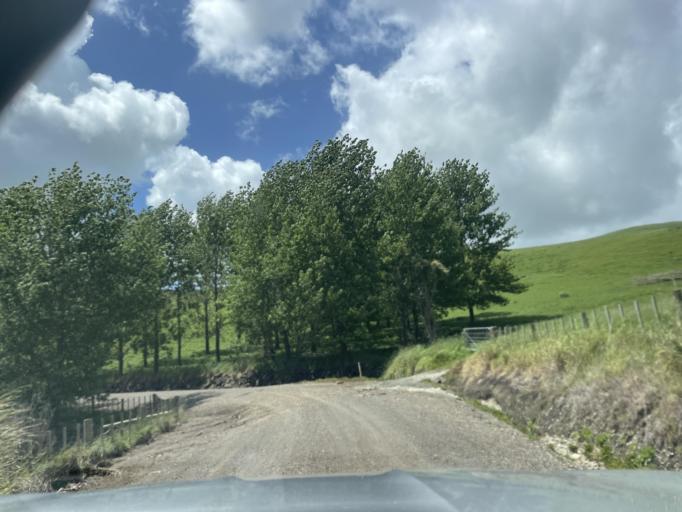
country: NZ
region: Auckland
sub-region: Auckland
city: Wellsford
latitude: -36.1884
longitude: 174.3233
